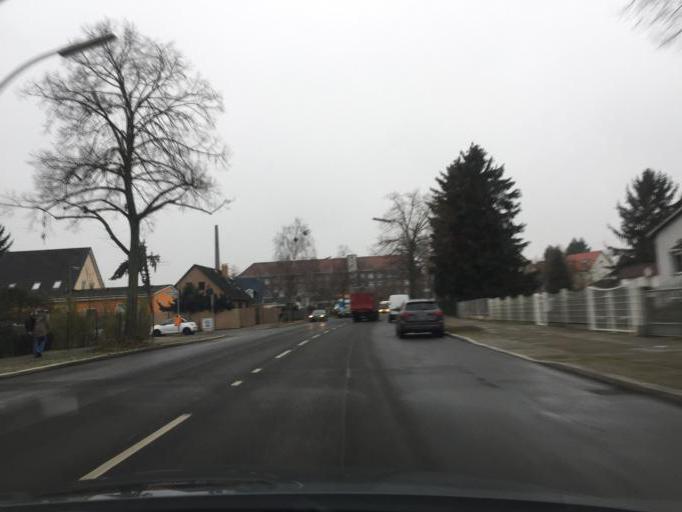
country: DE
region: Berlin
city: Mariendorf
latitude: 52.4210
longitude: 13.3874
